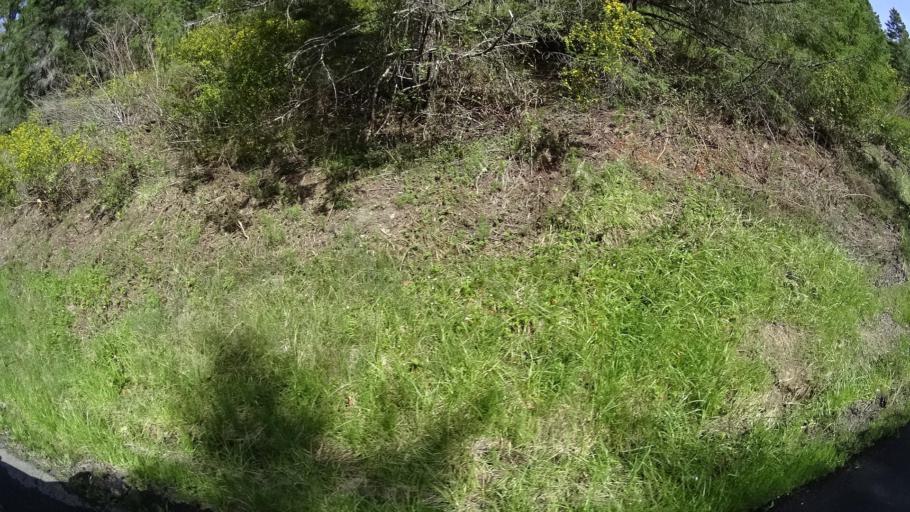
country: US
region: California
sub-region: Humboldt County
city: Redway
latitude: 40.4341
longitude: -123.7687
